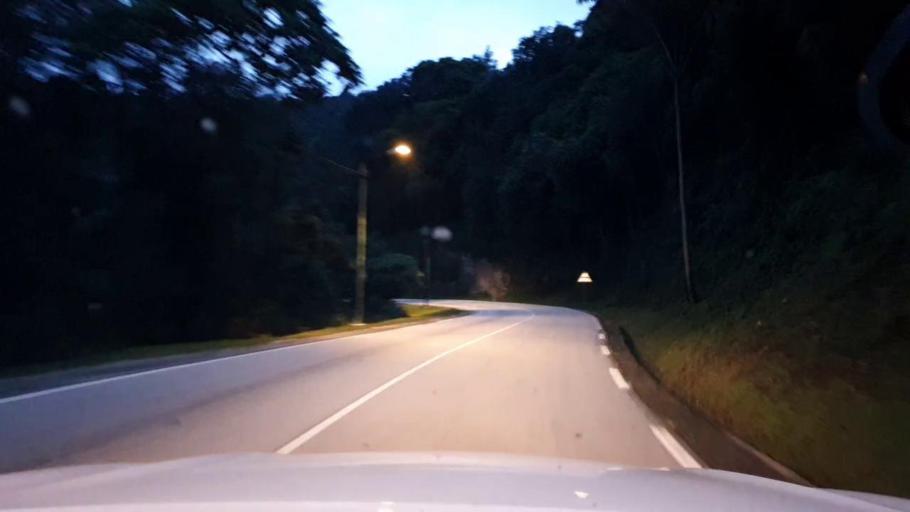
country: RW
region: Southern Province
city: Nzega
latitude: -2.5294
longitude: 29.3811
